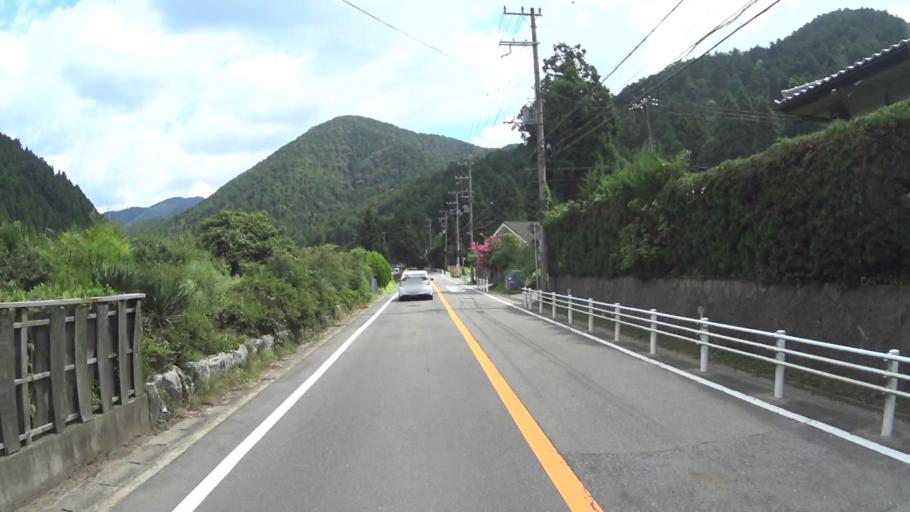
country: JP
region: Kyoto
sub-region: Kyoto-shi
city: Kamigyo-ku
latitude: 35.1093
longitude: 135.7966
